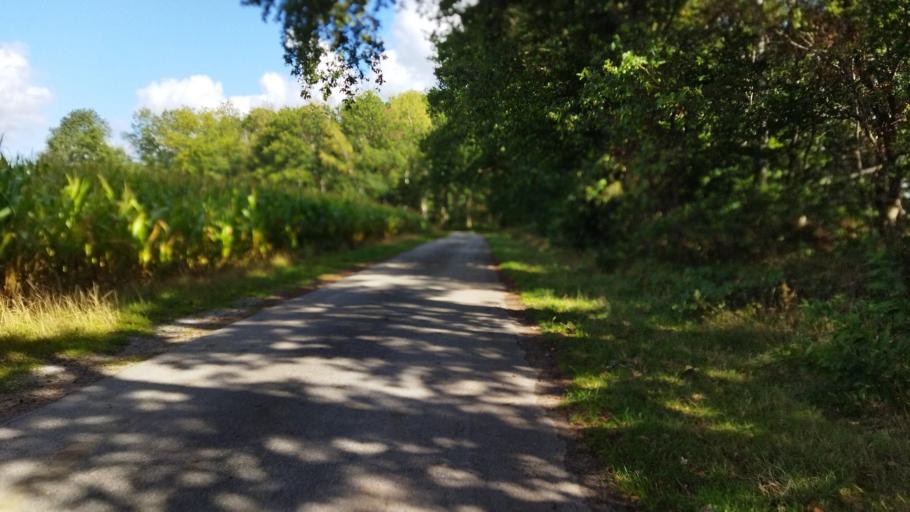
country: DE
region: Lower Saxony
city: Salzbergen
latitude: 52.3651
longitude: 7.3348
